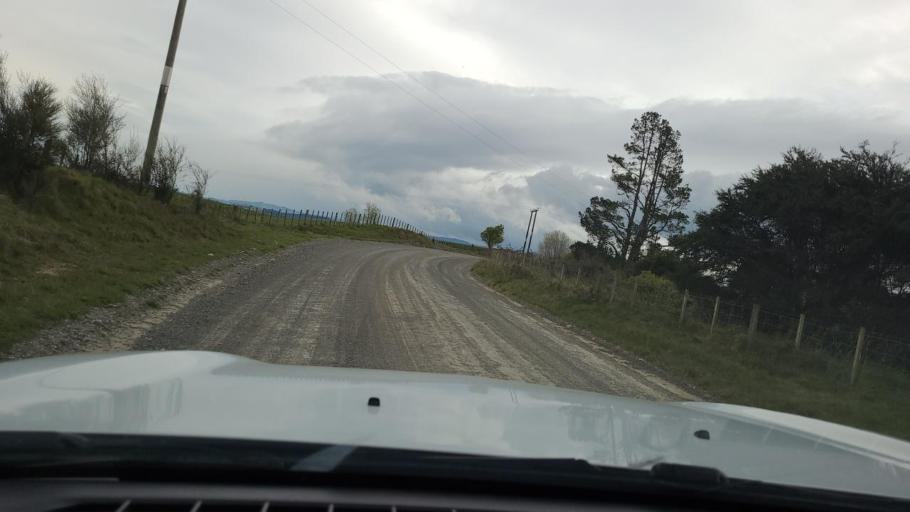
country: NZ
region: Hawke's Bay
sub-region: Napier City
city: Napier
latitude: -39.3184
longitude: 176.8402
